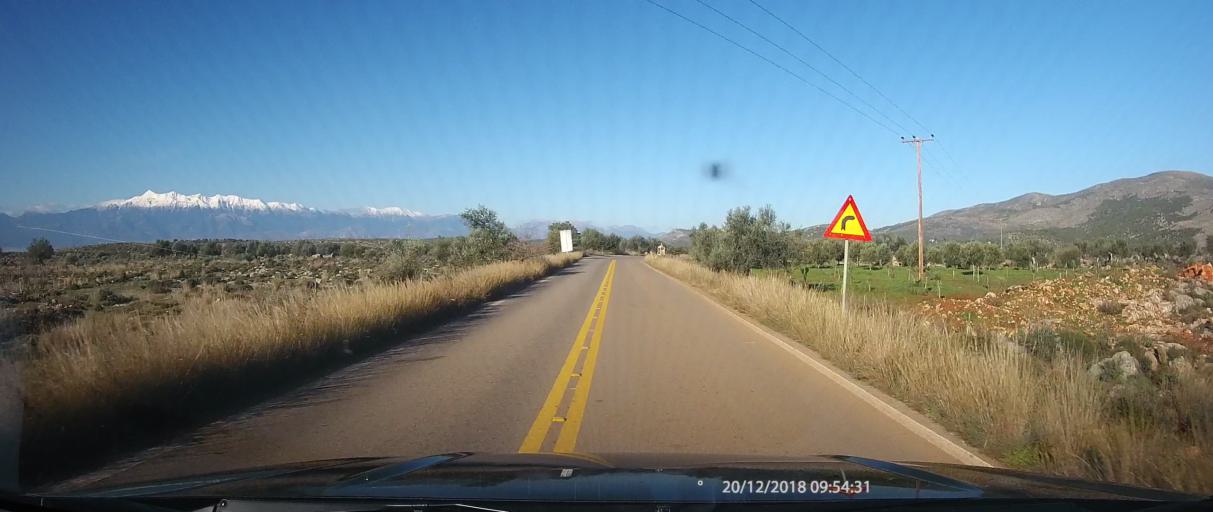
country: GR
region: Peloponnese
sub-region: Nomos Lakonias
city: Yerakion
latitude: 37.0172
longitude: 22.6348
